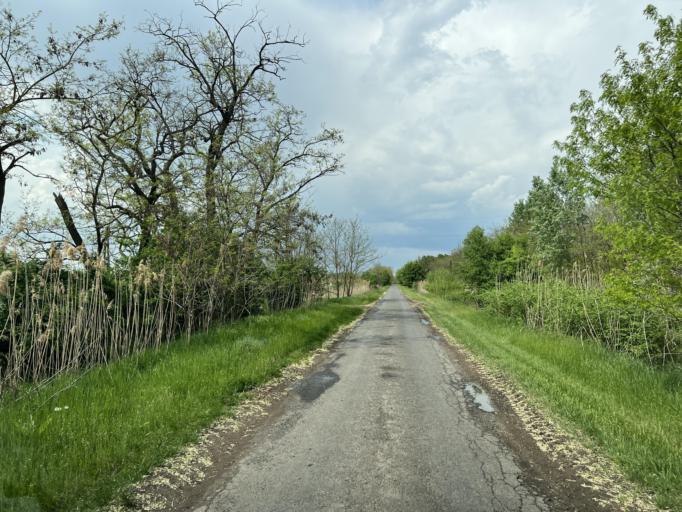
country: HU
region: Pest
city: Nagykoros
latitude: 46.9701
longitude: 19.8183
